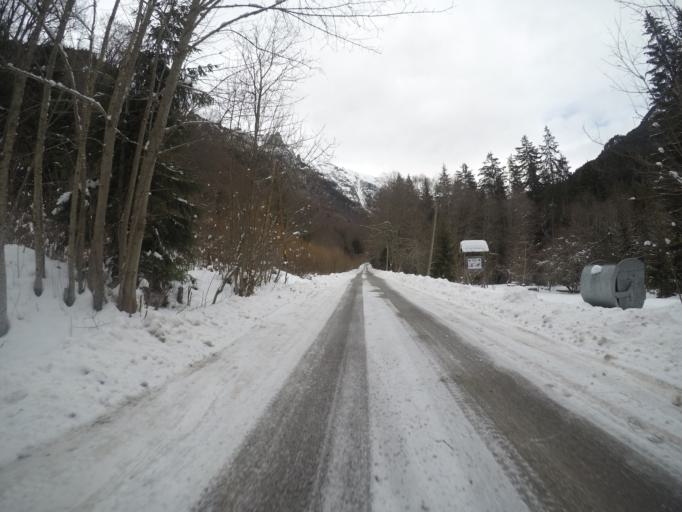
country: BG
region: Kyustendil
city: Sapareva Banya
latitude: 42.1468
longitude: 23.3688
